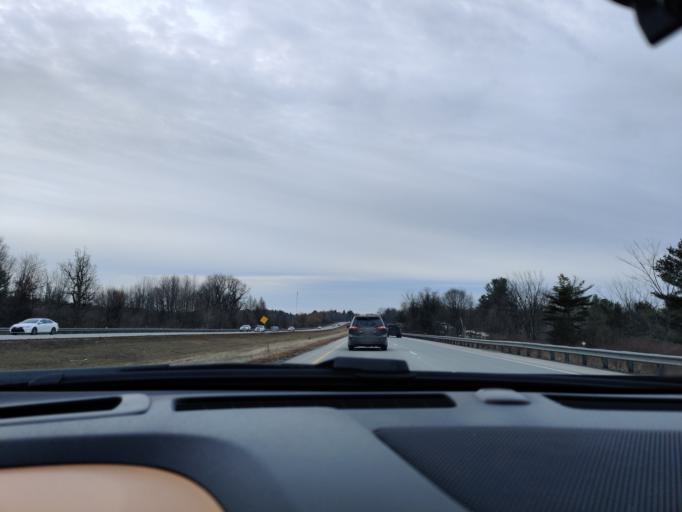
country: US
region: New York
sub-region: Jefferson County
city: Alexandria Bay
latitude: 44.3920
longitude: -75.9581
